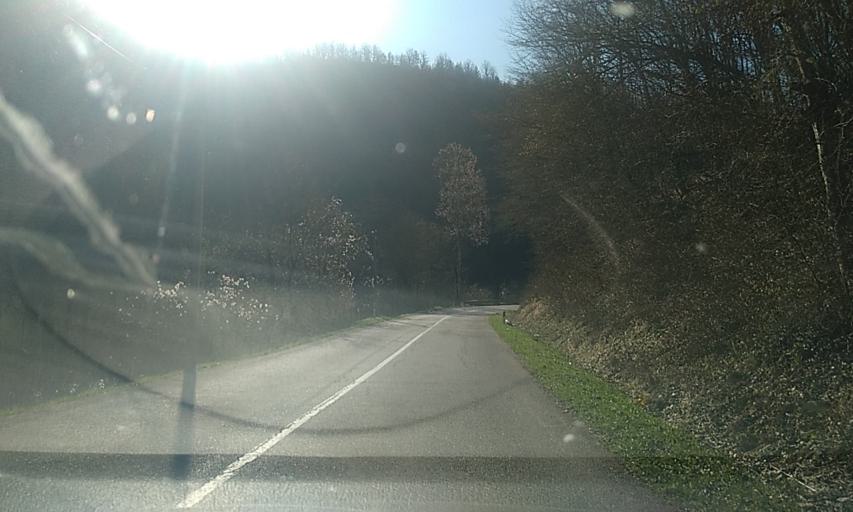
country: RS
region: Central Serbia
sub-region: Pcinjski Okrug
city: Bosilegrad
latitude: 42.4368
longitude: 22.5136
